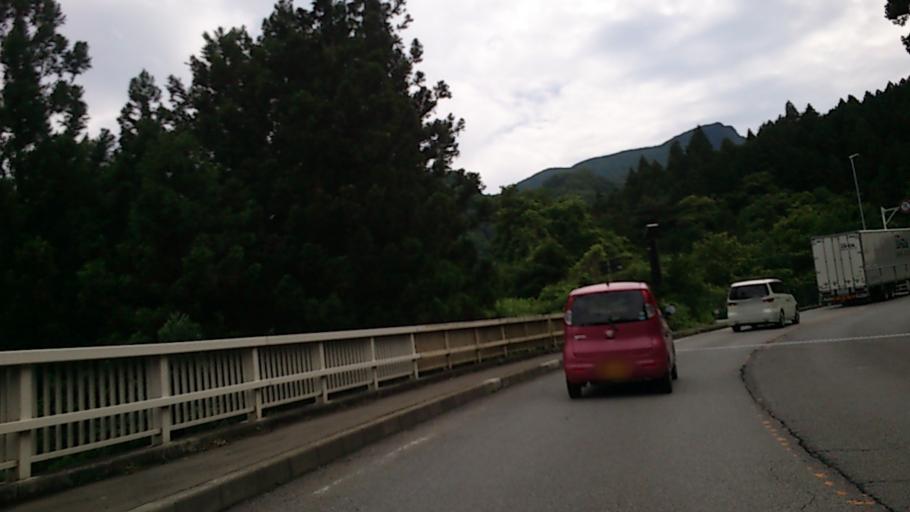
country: JP
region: Nagano
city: Saku
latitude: 36.2391
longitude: 138.6527
